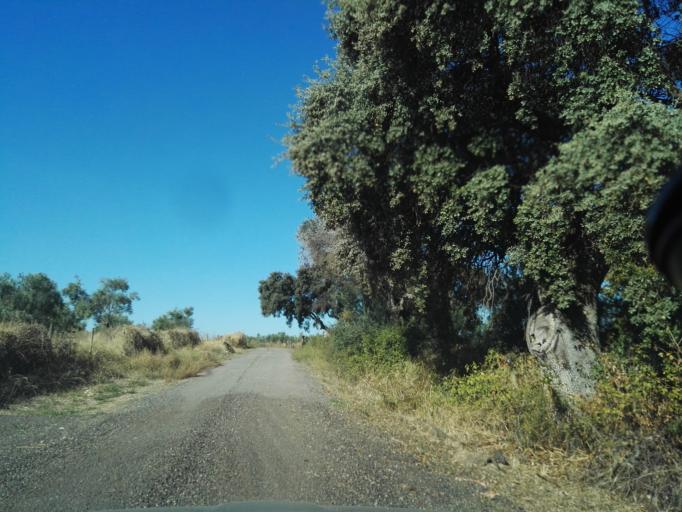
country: PT
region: Portalegre
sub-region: Elvas
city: Elvas
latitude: 38.9188
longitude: -7.1753
